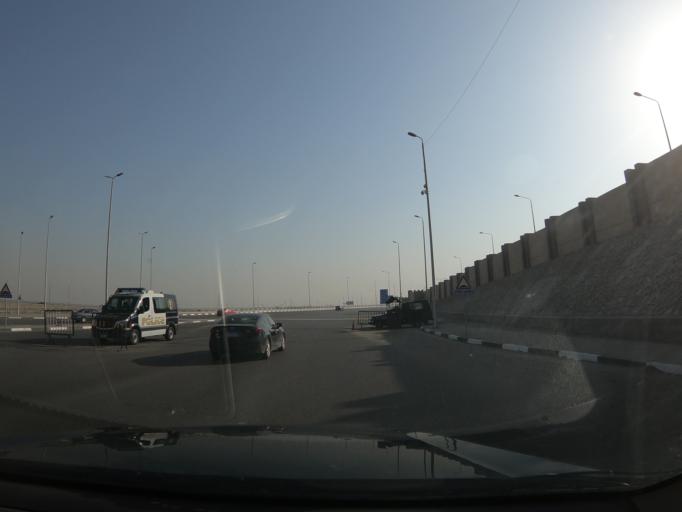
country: EG
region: Muhafazat al Qalyubiyah
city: Al Khankah
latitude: 30.1094
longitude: 31.3863
